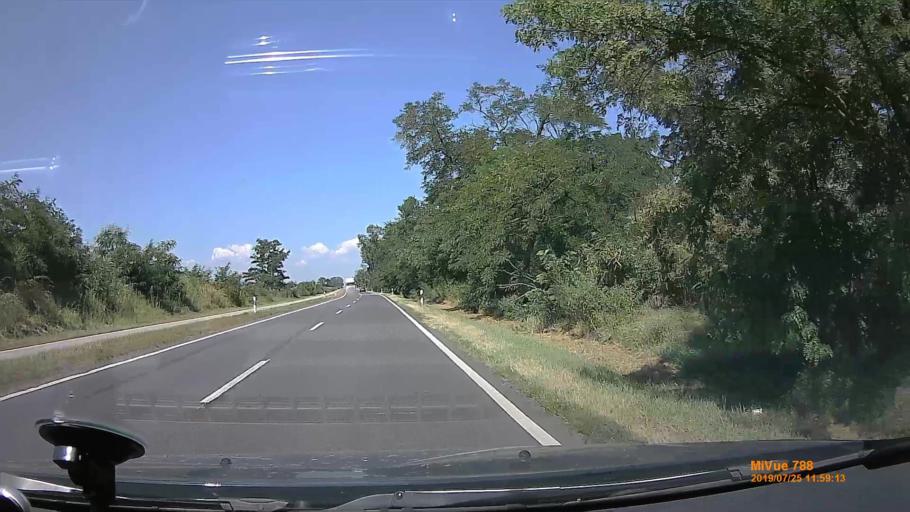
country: HU
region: Szabolcs-Szatmar-Bereg
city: Nyirtelek
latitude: 48.0241
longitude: 21.6106
